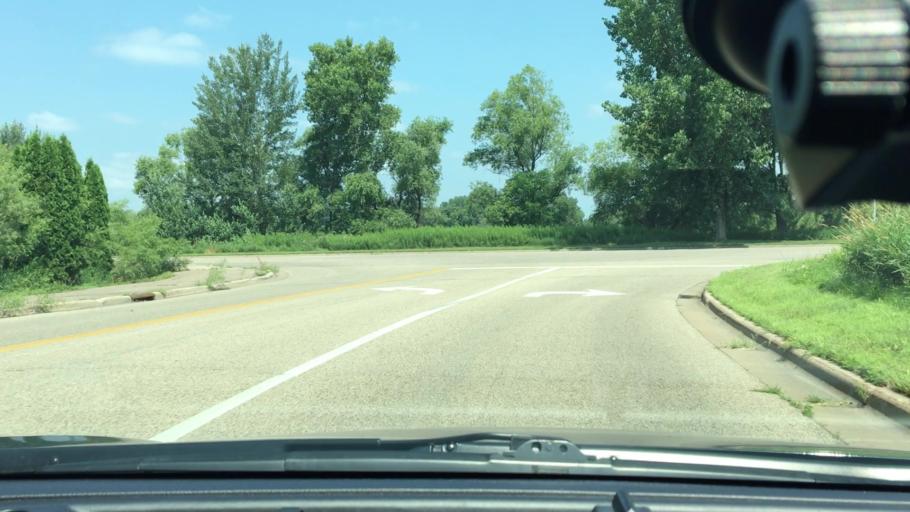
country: US
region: Minnesota
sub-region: Hennepin County
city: Plymouth
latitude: 44.9892
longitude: -93.4118
